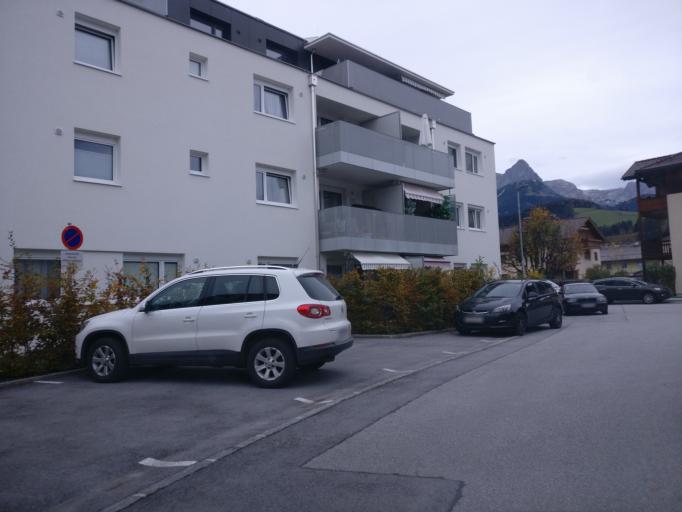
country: AT
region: Salzburg
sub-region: Politischer Bezirk Sankt Johann im Pongau
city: Bischofshofen
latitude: 47.4234
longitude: 13.2170
